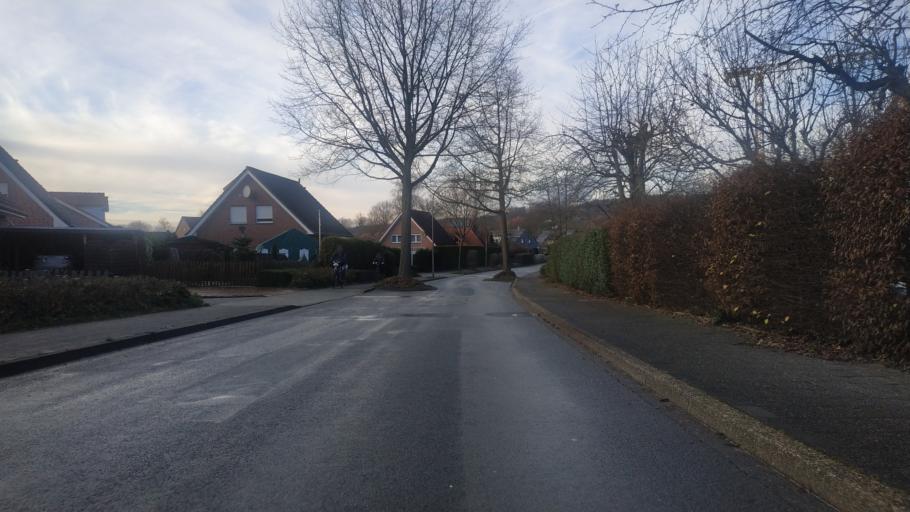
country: DE
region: North Rhine-Westphalia
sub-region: Regierungsbezirk Munster
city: Mettingen
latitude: 52.2696
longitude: 7.7759
